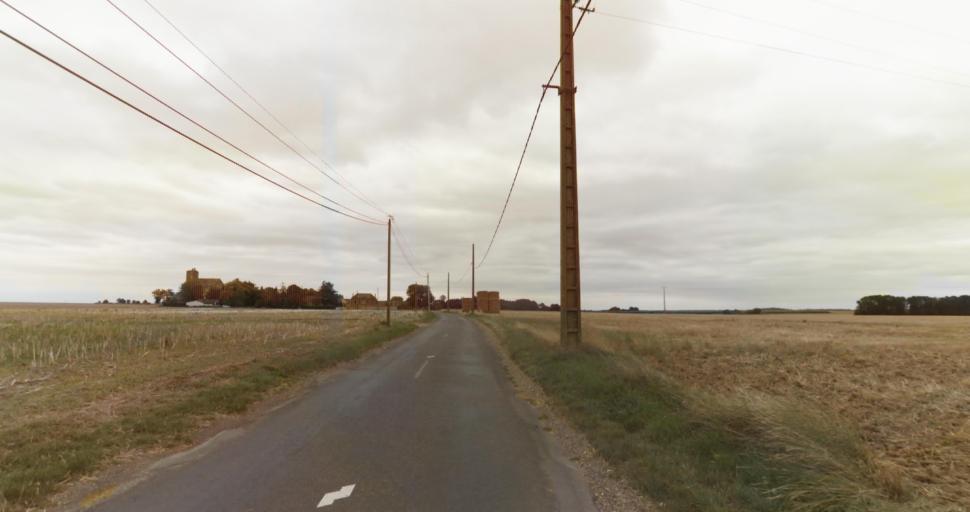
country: FR
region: Haute-Normandie
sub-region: Departement de l'Eure
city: Pacy-sur-Eure
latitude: 48.9459
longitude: 1.3103
